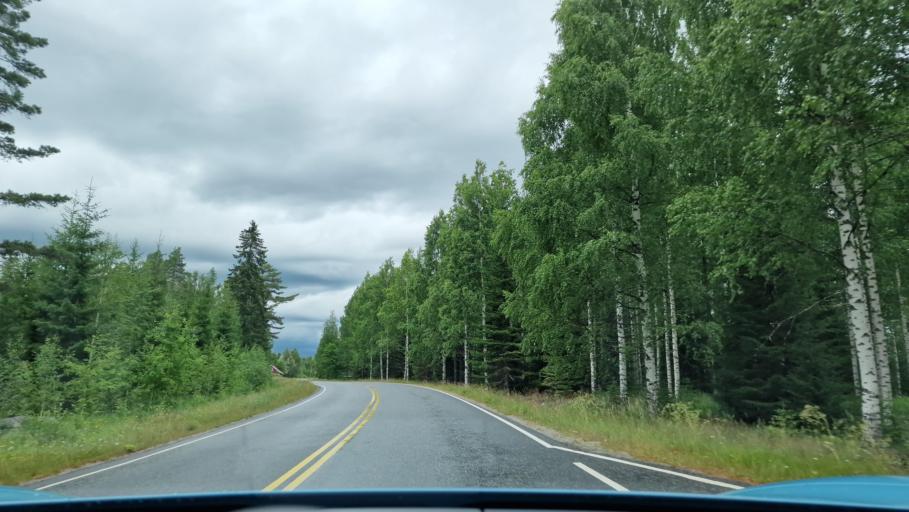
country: FI
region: Southern Ostrobothnia
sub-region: Jaerviseutu
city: Soini
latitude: 62.6946
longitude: 24.4579
